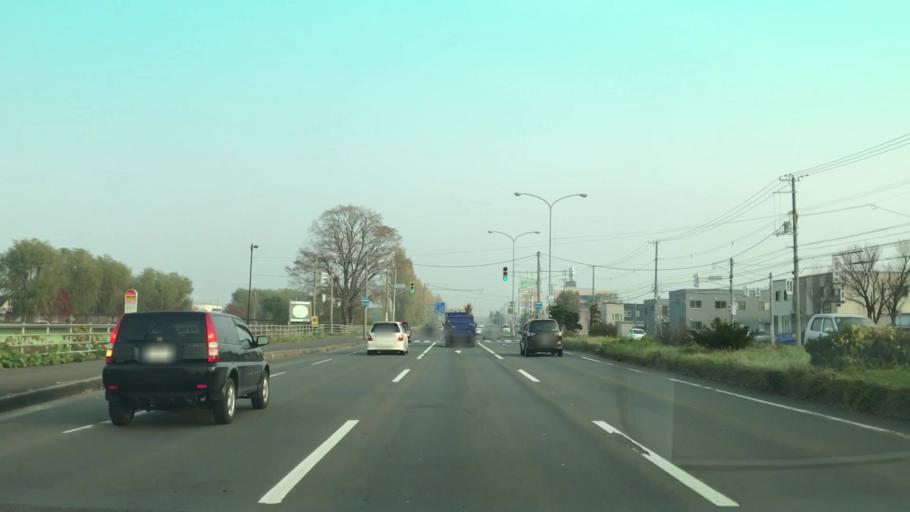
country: JP
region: Hokkaido
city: Ishikari
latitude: 43.1542
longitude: 141.3518
